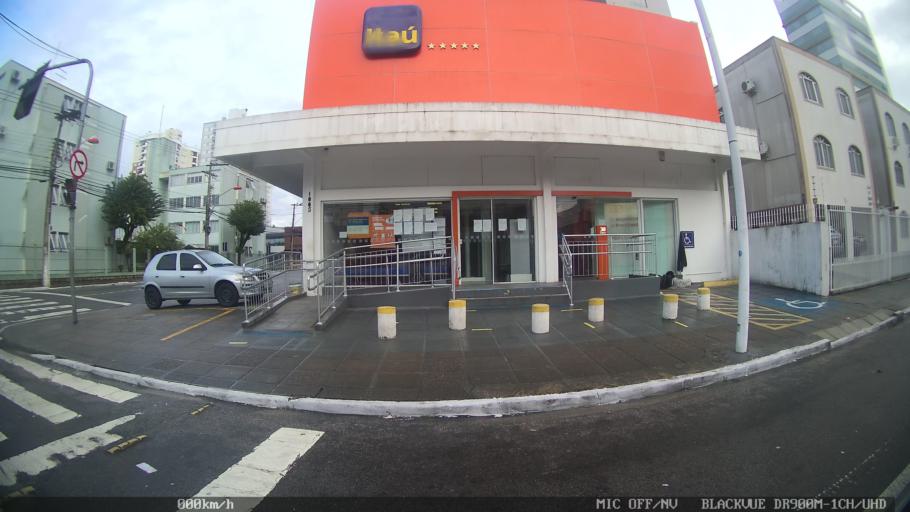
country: BR
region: Santa Catarina
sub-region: Sao Jose
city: Campinas
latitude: -27.5922
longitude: -48.6131
